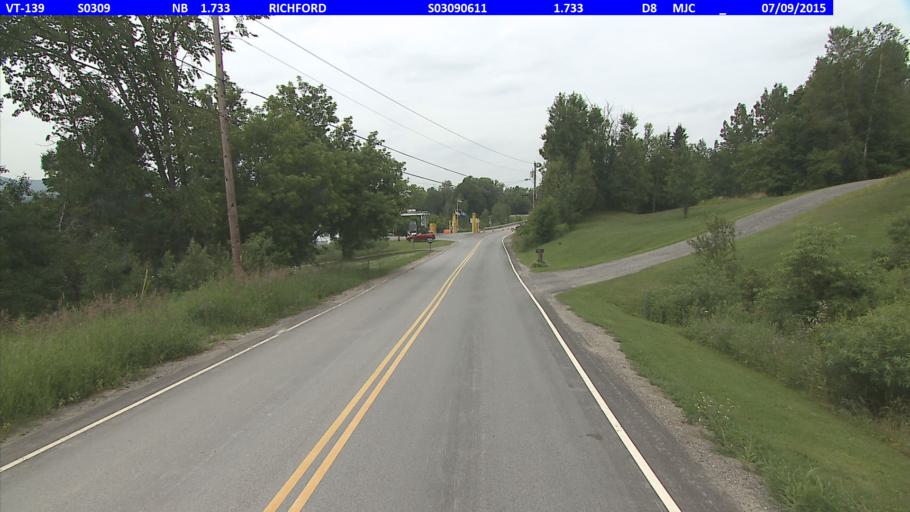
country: US
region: Vermont
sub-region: Franklin County
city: Richford
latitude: 45.0128
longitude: -72.6621
